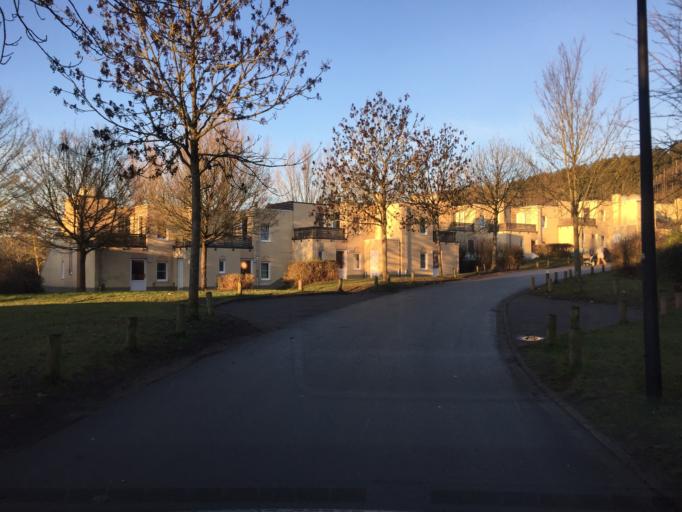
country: DE
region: North Rhine-Westphalia
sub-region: Regierungsbezirk Arnsberg
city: Medebach
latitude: 51.2084
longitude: 8.6863
